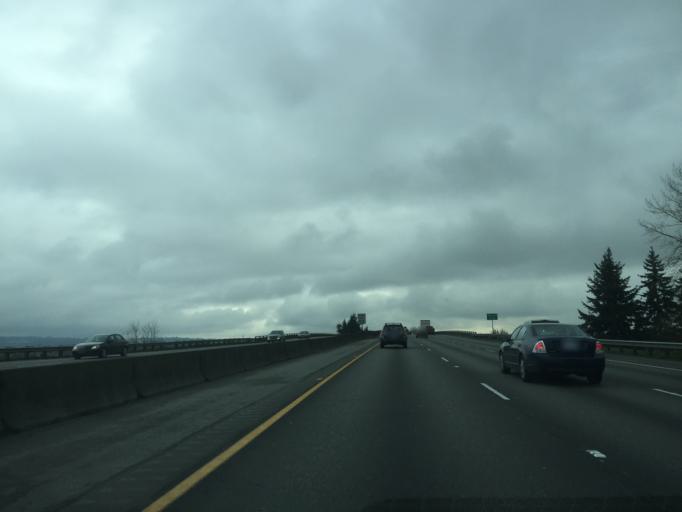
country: US
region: Washington
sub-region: Snohomish County
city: Marysville
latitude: 48.0387
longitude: -122.1788
